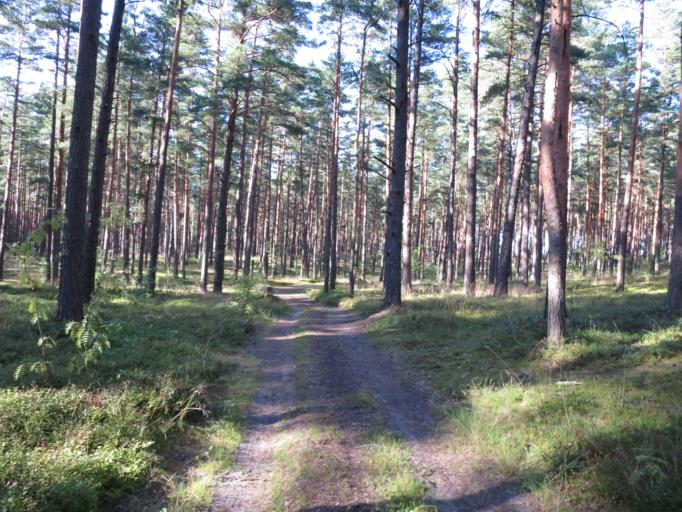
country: LV
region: Riga
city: Jaunciems
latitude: 57.0772
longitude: 24.2000
